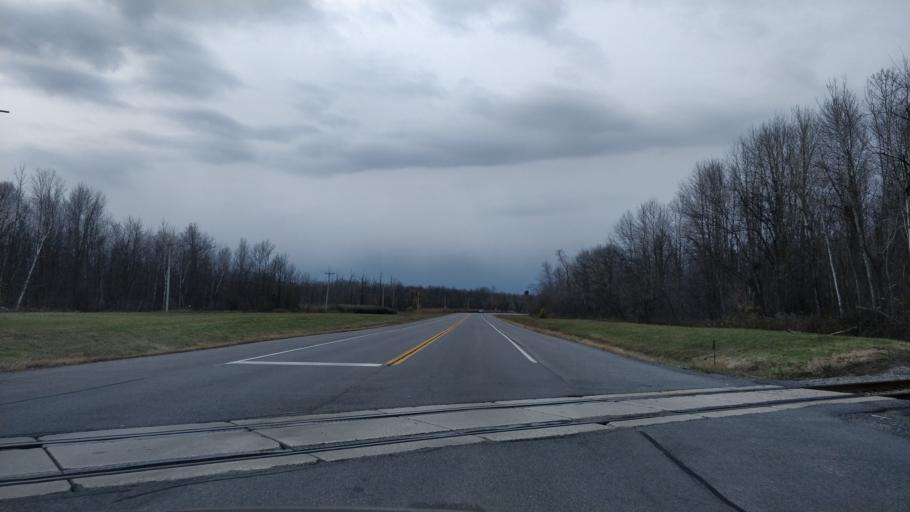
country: US
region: New York
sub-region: St. Lawrence County
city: Ogdensburg
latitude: 44.7099
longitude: -75.4512
